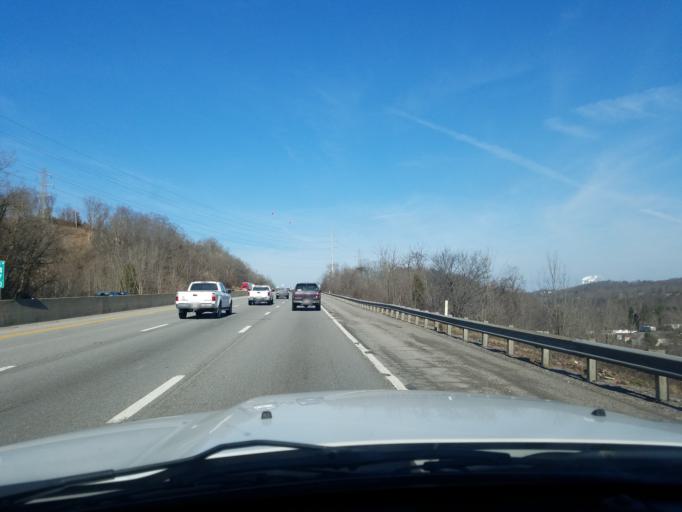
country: US
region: West Virginia
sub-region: Kanawha County
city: Cross Lanes
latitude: 38.4178
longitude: -81.8006
